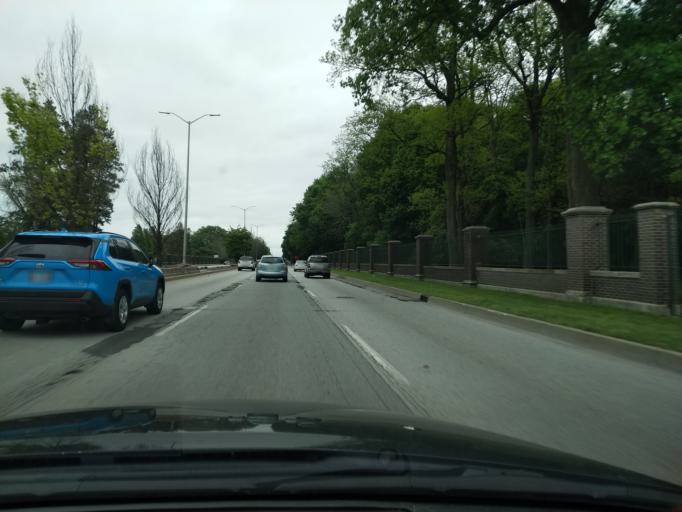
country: US
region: Indiana
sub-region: Marion County
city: Broad Ripple
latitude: 39.8247
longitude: -86.1760
